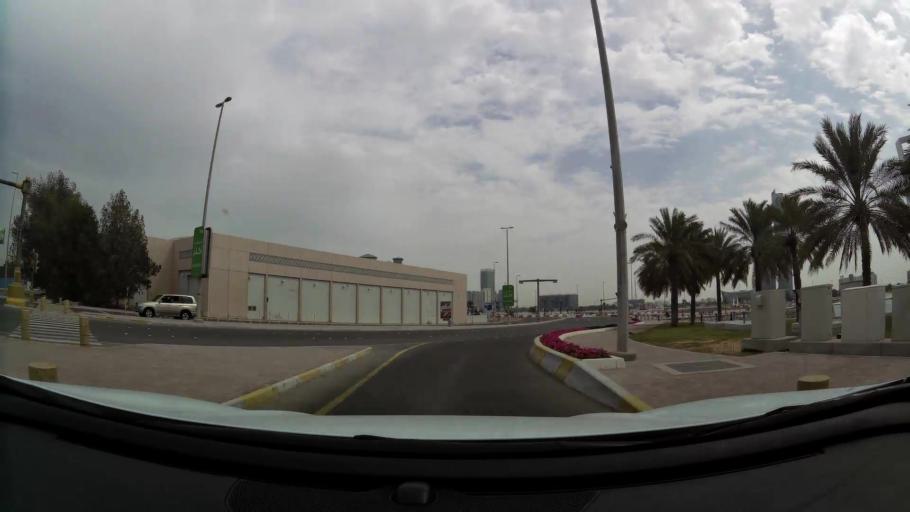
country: AE
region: Abu Dhabi
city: Abu Dhabi
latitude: 24.4719
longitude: 54.3203
